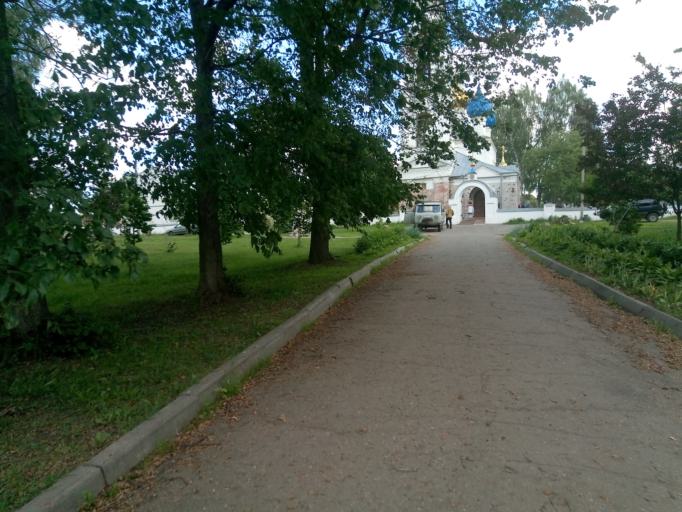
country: RU
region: Jaroslavl
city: Yaroslavl
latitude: 57.6584
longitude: 39.9555
